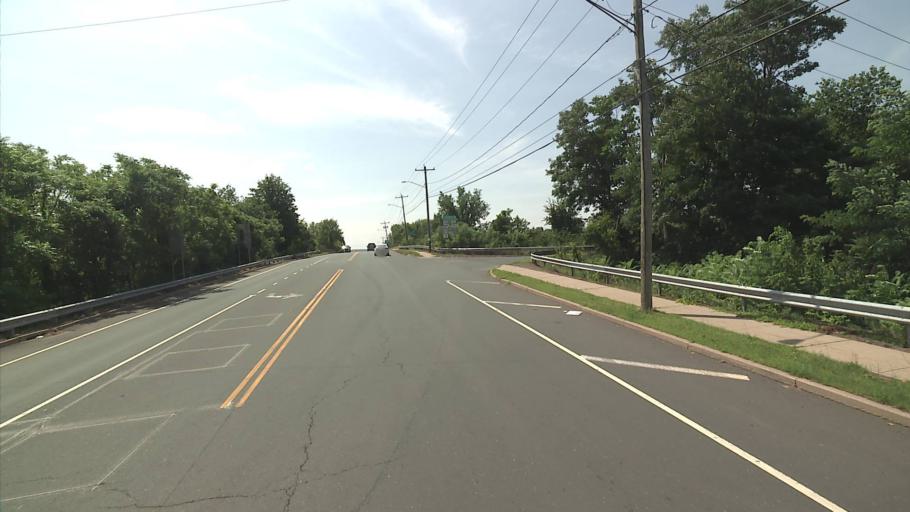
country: US
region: Connecticut
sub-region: Hartford County
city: Kensington
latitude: 41.6476
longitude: -72.7712
